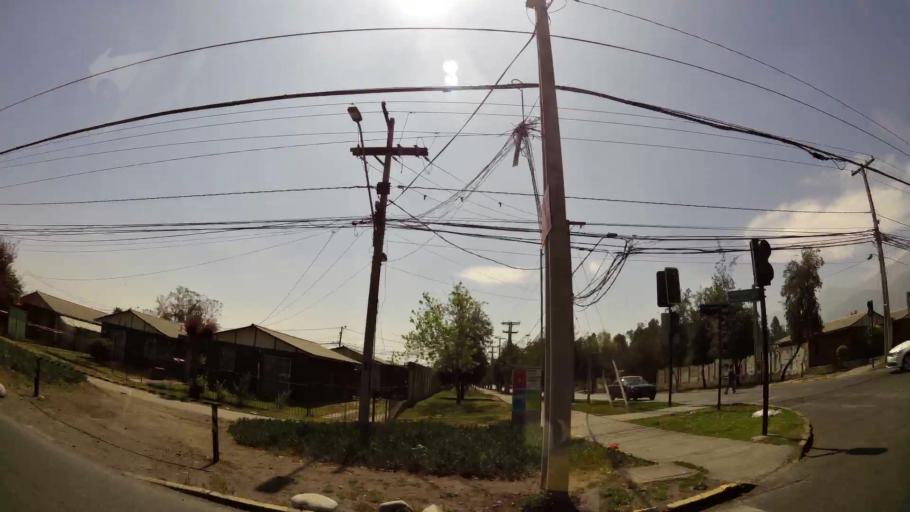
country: CL
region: Santiago Metropolitan
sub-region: Provincia de Santiago
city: Villa Presidente Frei, Nunoa, Santiago, Chile
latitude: -33.4628
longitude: -70.5418
